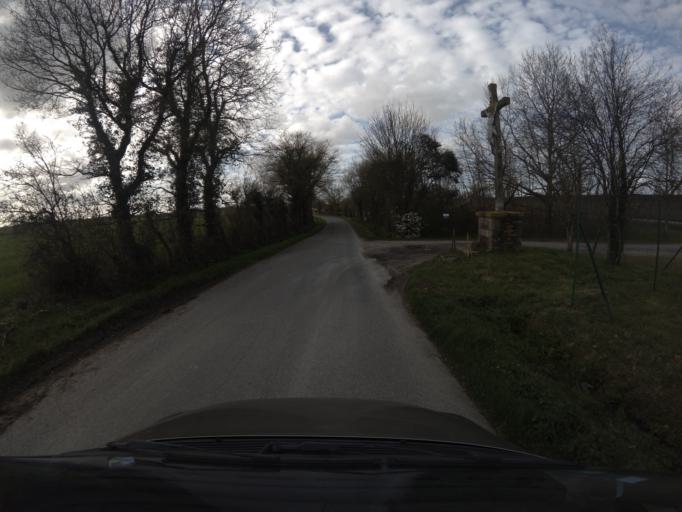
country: FR
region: Pays de la Loire
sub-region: Departement de la Vendee
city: Bouffere
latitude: 46.9664
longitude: -1.3522
